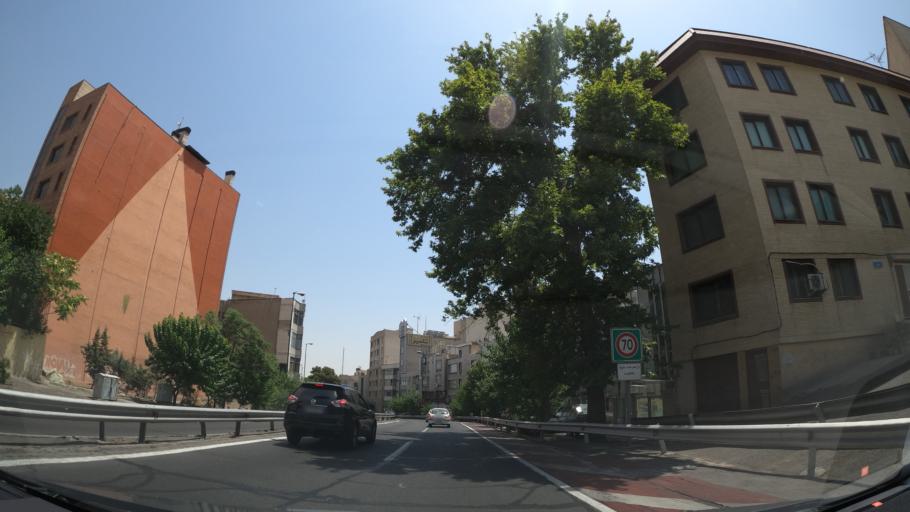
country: IR
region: Tehran
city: Tehran
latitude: 35.7226
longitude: 51.4252
